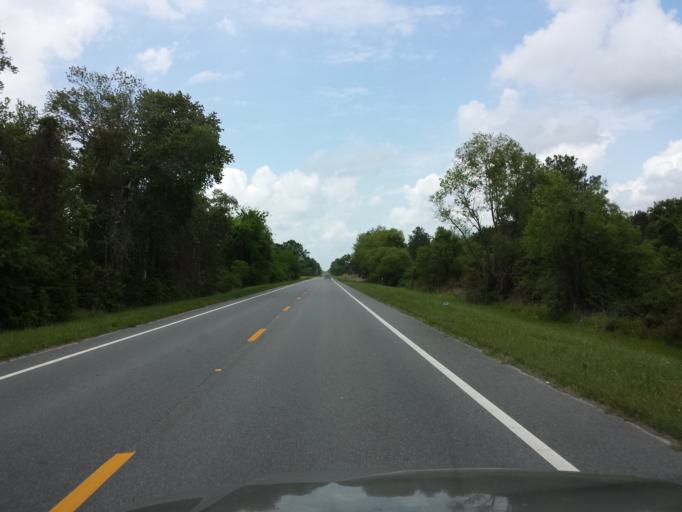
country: US
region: Florida
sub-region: Hamilton County
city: Jasper
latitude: 30.4569
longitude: -82.8929
